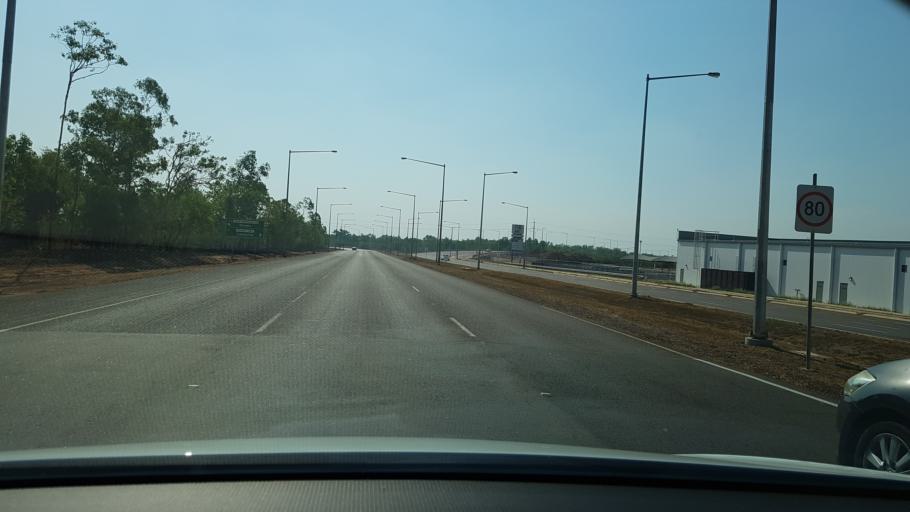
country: AU
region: Northern Territory
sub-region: Palmerston
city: Palmerston
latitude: -12.4704
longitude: 130.9804
